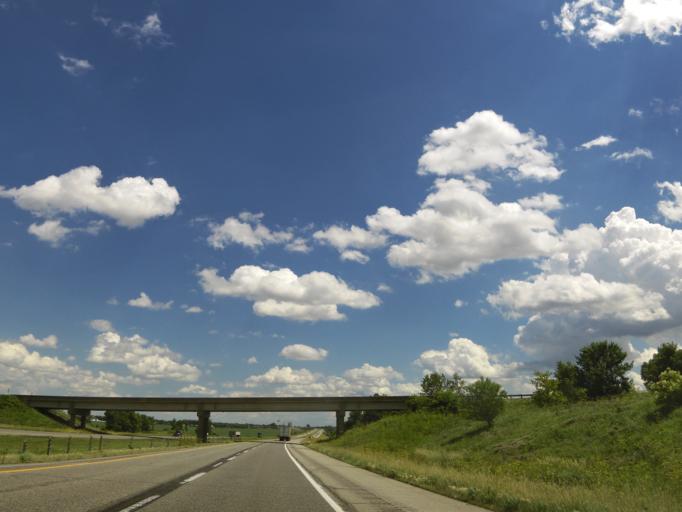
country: US
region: Iowa
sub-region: Linn County
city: Center Point
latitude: 42.1863
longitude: -91.8022
